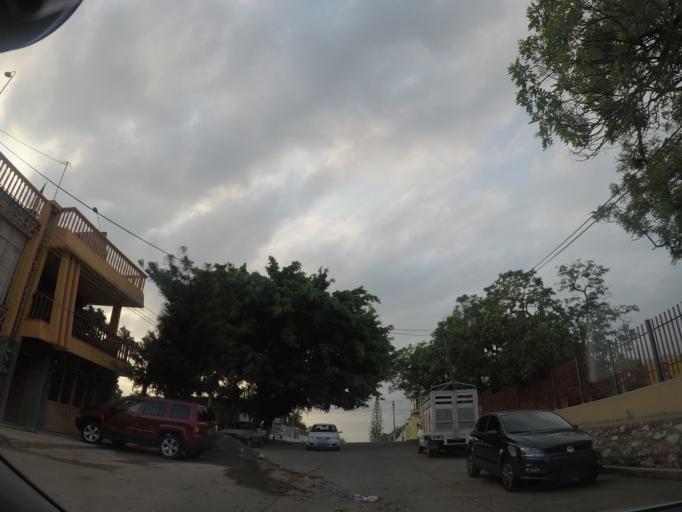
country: MX
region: Oaxaca
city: Matias Romero
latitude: 16.8750
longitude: -95.0423
